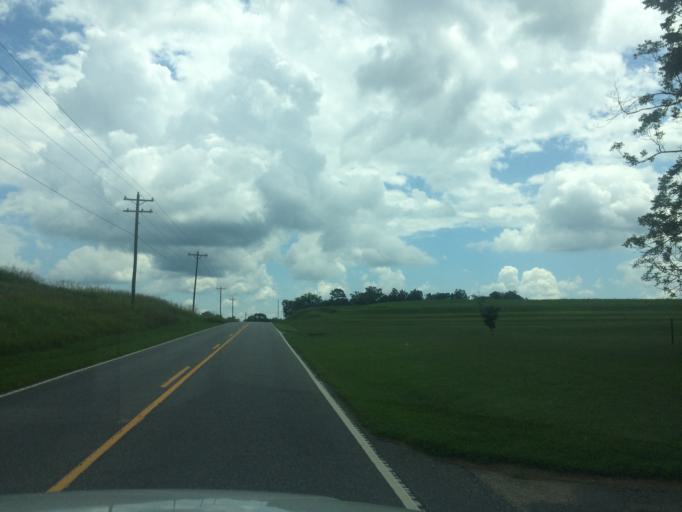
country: US
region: South Carolina
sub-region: Spartanburg County
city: Landrum
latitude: 35.2241
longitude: -82.0540
